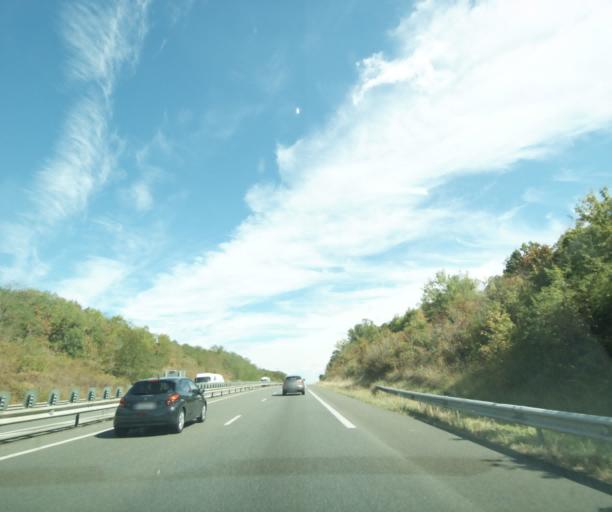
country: FR
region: Midi-Pyrenees
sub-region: Departement du Tarn-et-Garonne
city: Auvillar
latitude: 44.0598
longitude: 0.9030
